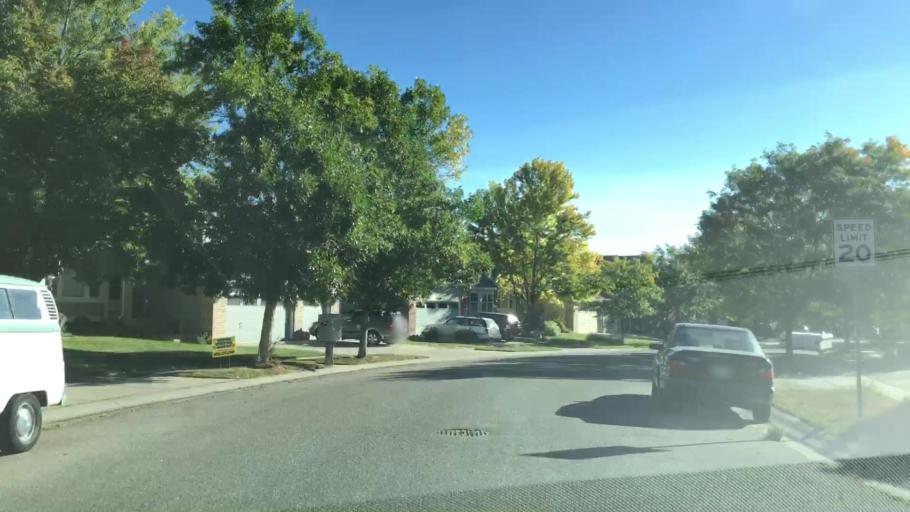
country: US
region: Colorado
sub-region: Larimer County
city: Loveland
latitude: 40.3986
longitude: -105.1311
